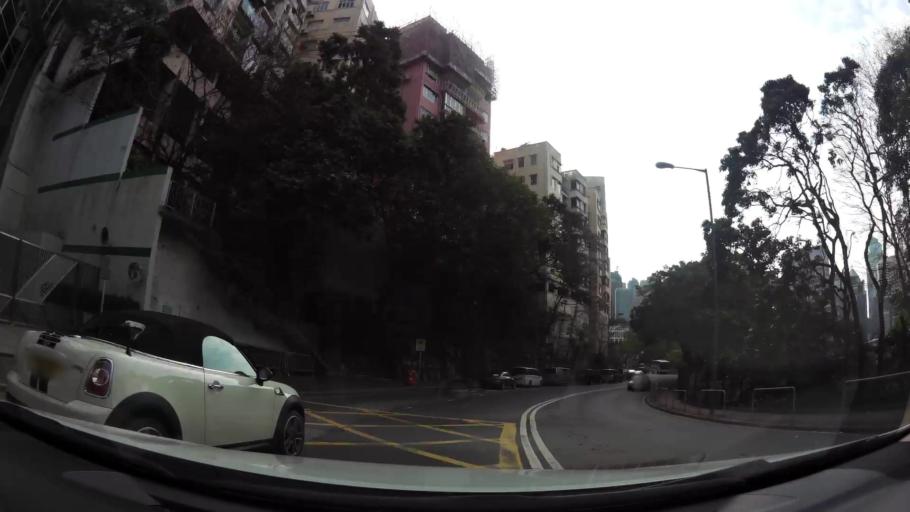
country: HK
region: Central and Western
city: Central
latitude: 22.2758
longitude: 114.1612
